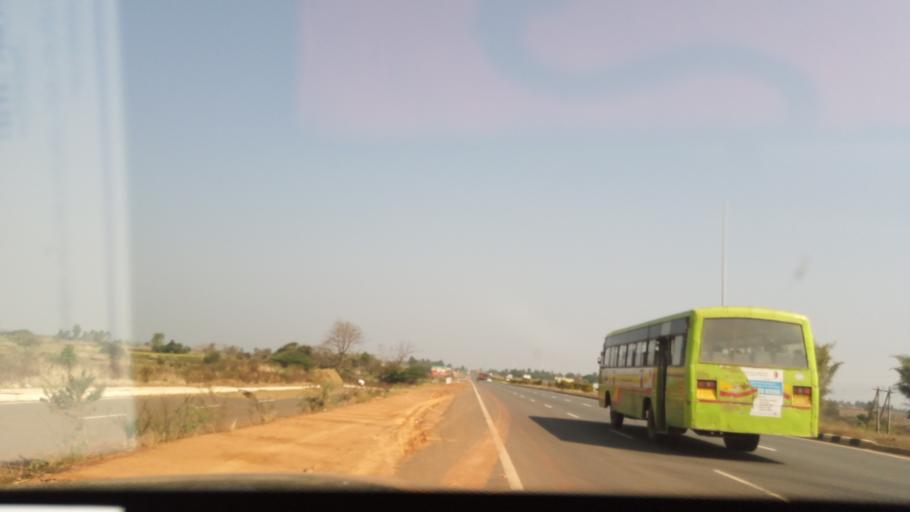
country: IN
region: Karnataka
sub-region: Haveri
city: Shiggaon
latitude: 15.0890
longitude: 75.1522
